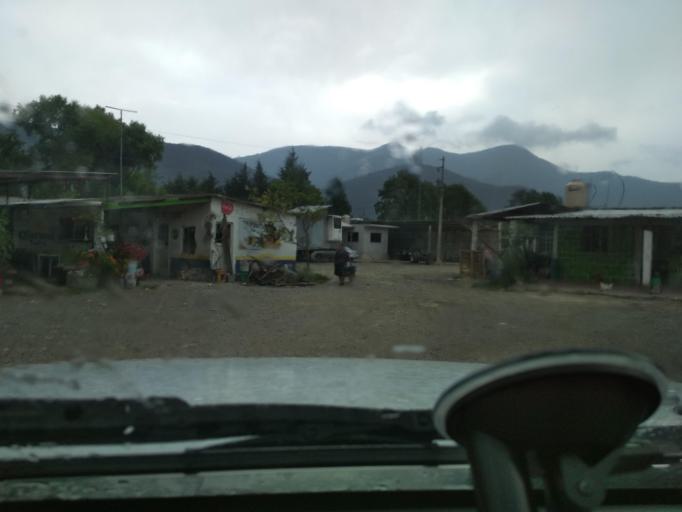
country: MX
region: Veracruz
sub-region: Nogales
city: Taza de Agua Ojo Zarco
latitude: 18.7719
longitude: -97.2168
